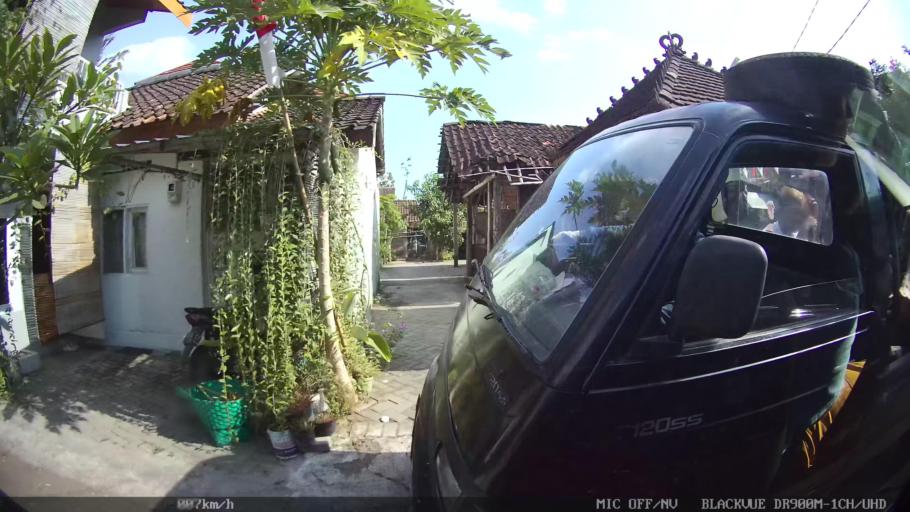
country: ID
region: Daerah Istimewa Yogyakarta
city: Sewon
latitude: -7.8344
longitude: 110.4062
